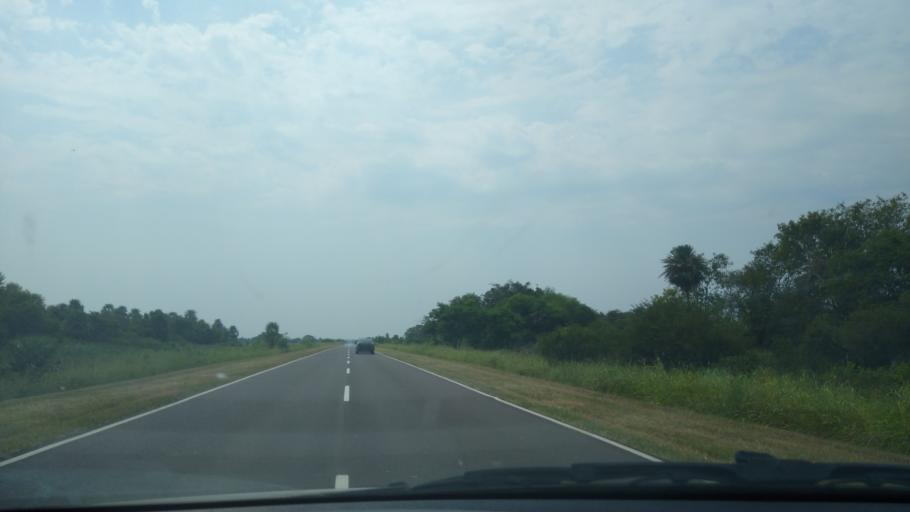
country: AR
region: Chaco
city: La Eduvigis
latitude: -27.0044
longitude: -58.9717
